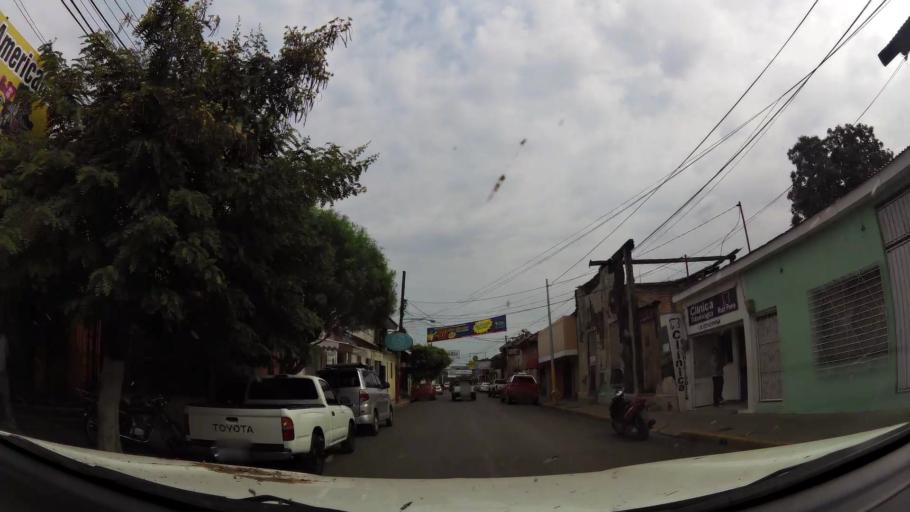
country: NI
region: Masaya
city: Masaya
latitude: 11.9766
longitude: -86.0959
